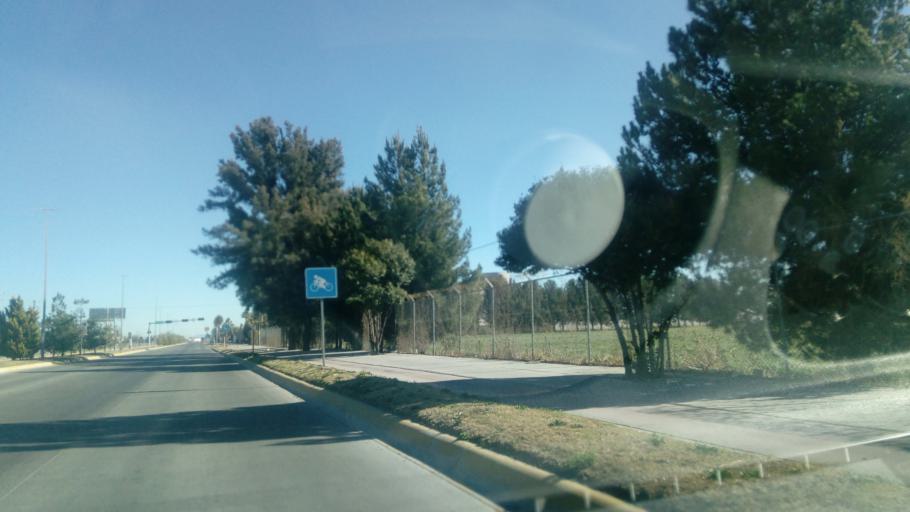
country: MX
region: Durango
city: Victoria de Durango
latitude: 24.0798
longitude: -104.5883
